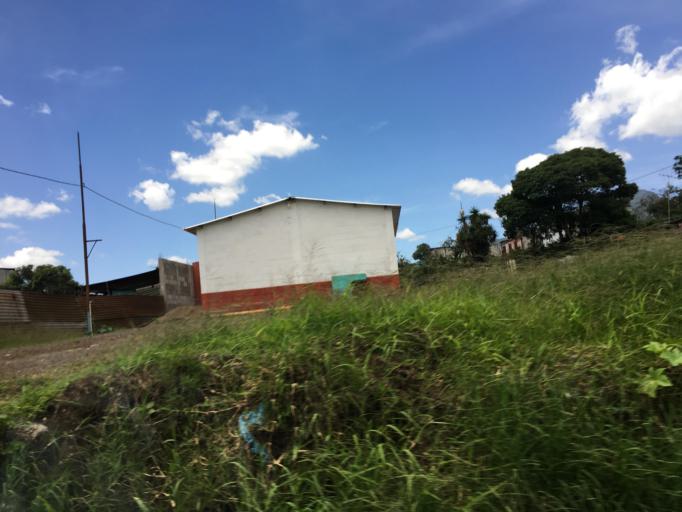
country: GT
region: Sacatepequez
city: Ciudad Vieja
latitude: 14.5239
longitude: -90.7534
